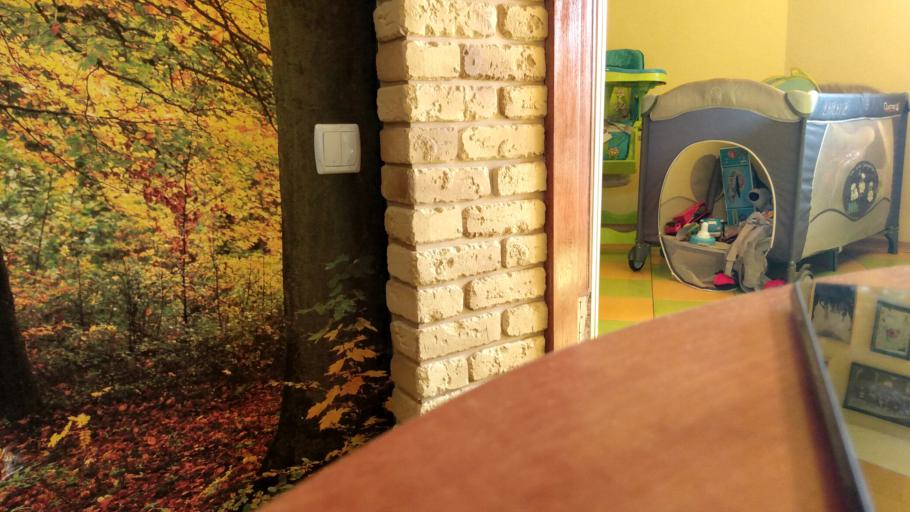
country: RU
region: Tverskaya
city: Emmaus
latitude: 56.8495
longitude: 36.1507
